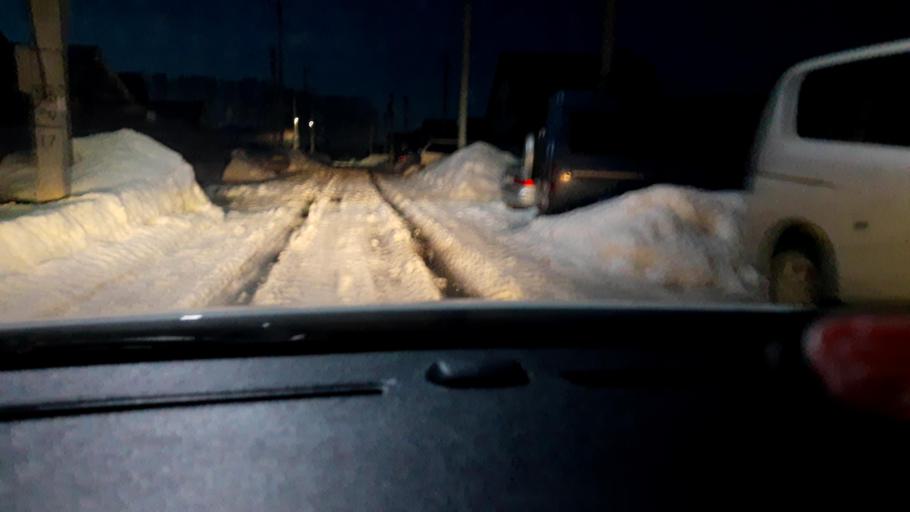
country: RU
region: Bashkortostan
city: Ufa
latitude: 54.5463
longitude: 55.9304
